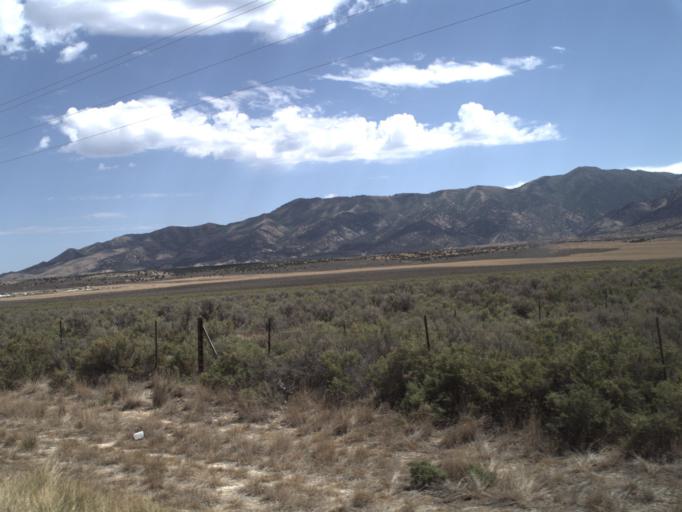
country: US
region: Utah
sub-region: Tooele County
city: Tooele
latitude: 40.3896
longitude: -112.3862
